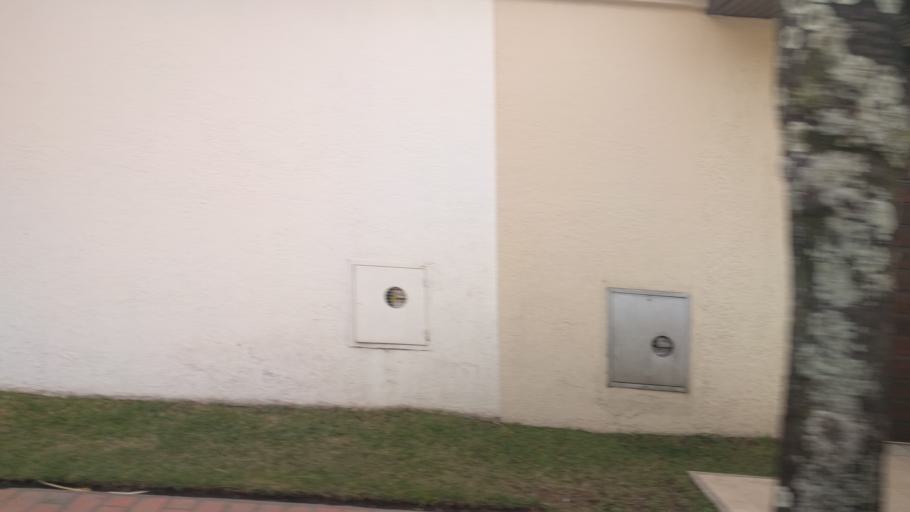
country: BO
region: Santa Cruz
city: Santa Cruz de la Sierra
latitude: -17.8035
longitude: -63.2061
